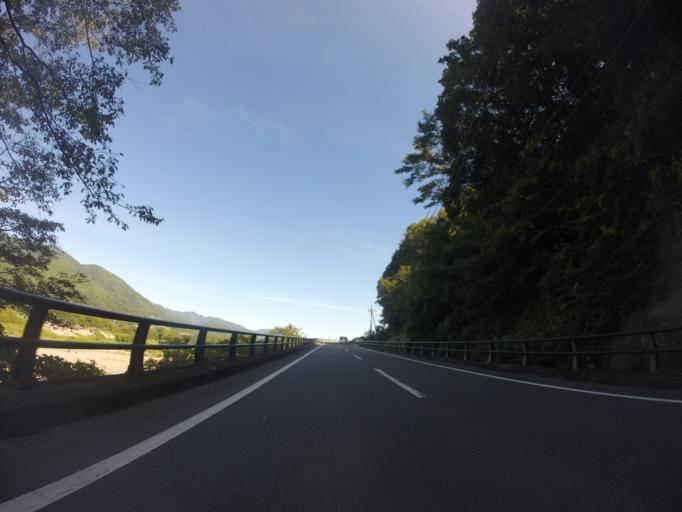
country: JP
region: Shizuoka
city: Fujinomiya
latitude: 35.2981
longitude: 138.4563
